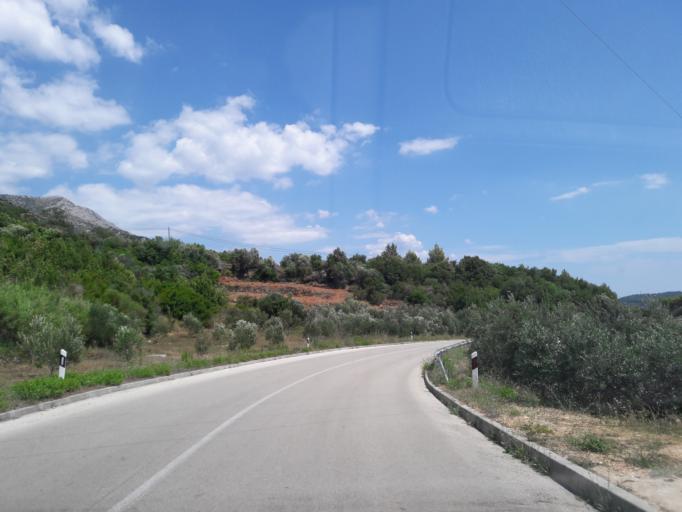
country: HR
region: Dubrovacko-Neretvanska
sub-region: Grad Korcula
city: Zrnovo
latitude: 42.9860
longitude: 17.0969
